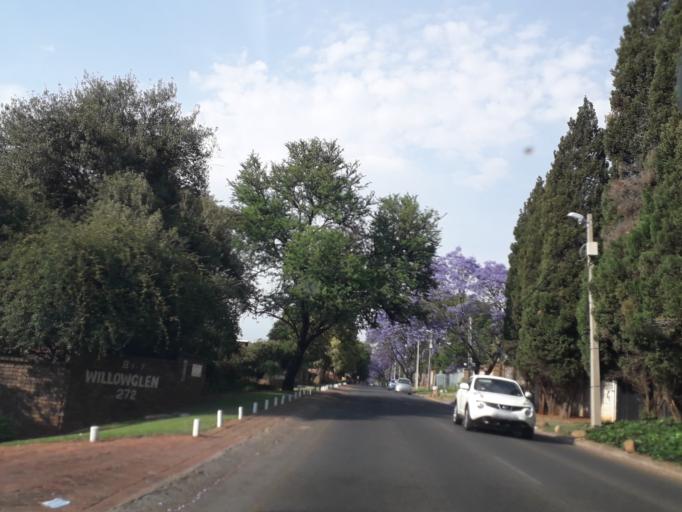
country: ZA
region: Gauteng
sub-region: City of Johannesburg Metropolitan Municipality
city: Roodepoort
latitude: -26.1229
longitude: 27.9560
